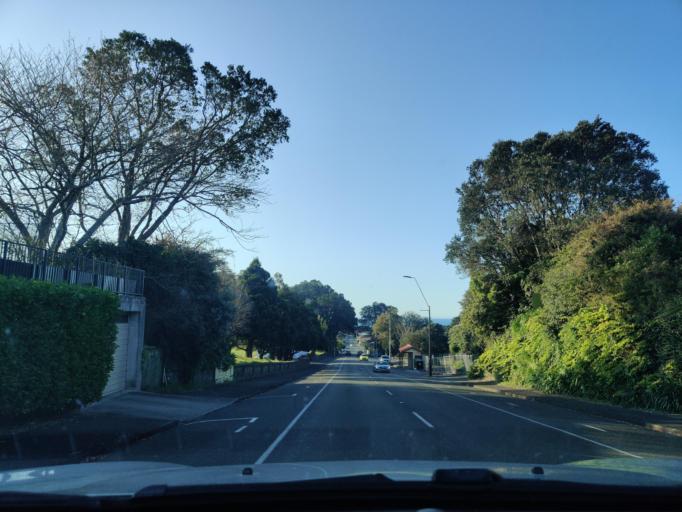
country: NZ
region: Taranaki
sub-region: New Plymouth District
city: New Plymouth
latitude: -39.0659
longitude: 174.0655
